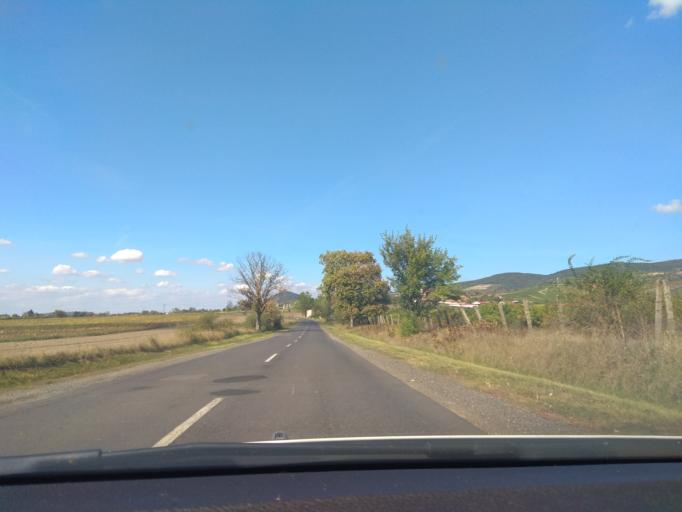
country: HU
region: Borsod-Abauj-Zemplen
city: Tallya
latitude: 48.2239
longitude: 21.2389
